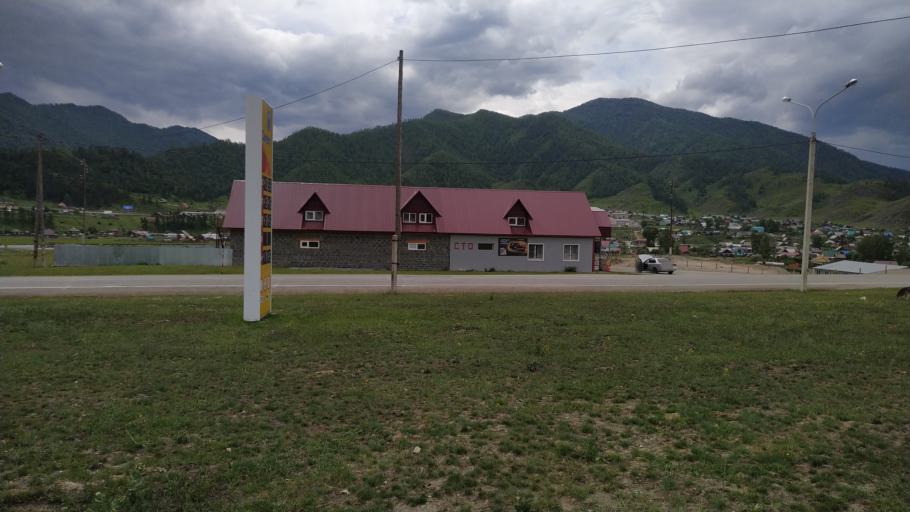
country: RU
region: Altay
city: Onguday
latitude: 50.7460
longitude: 86.1556
